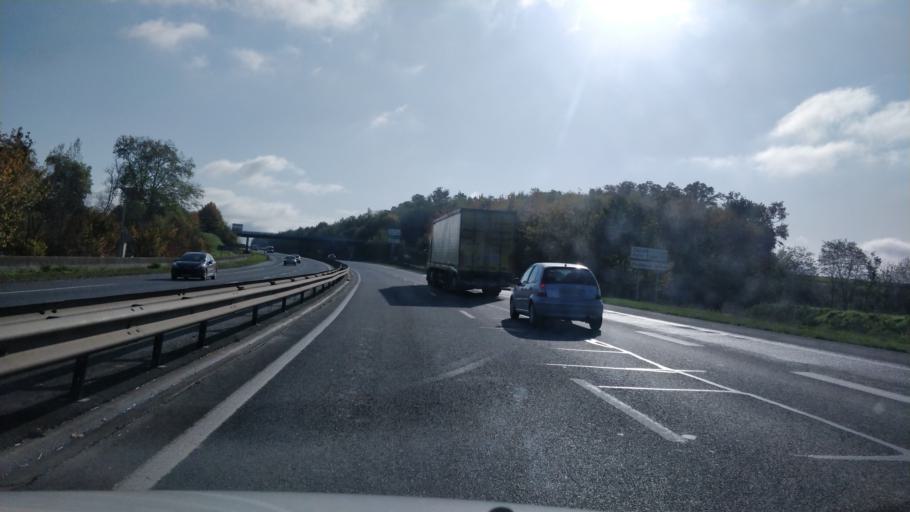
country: FR
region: Lower Normandy
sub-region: Departement du Calvados
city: Bretteville-sur-Odon
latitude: 49.1587
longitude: -0.4262
